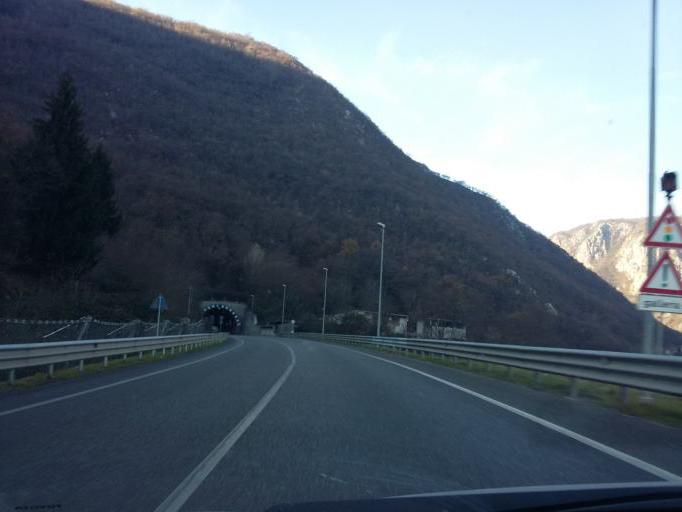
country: IT
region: Lombardy
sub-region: Provincia di Brescia
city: Vobarno
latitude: 45.6408
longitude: 10.4931
